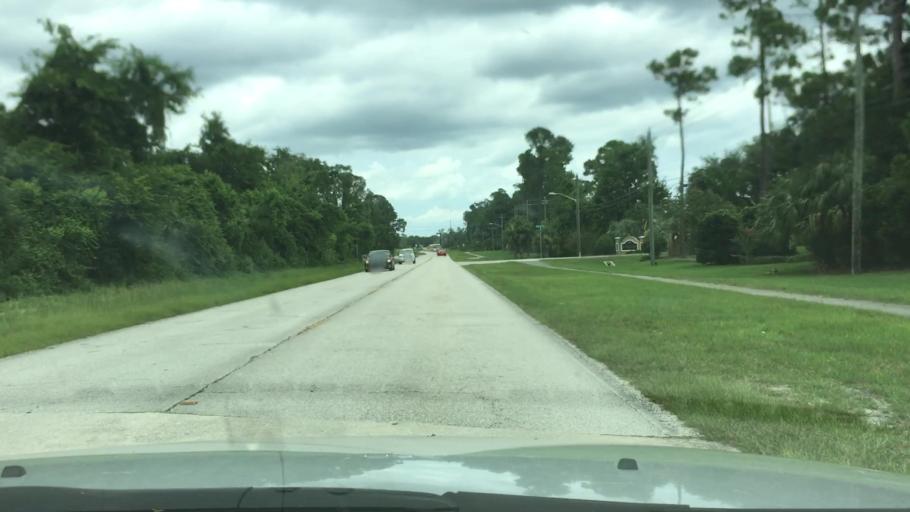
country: US
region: Florida
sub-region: Volusia County
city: Holly Hill
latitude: 29.2273
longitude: -81.0704
